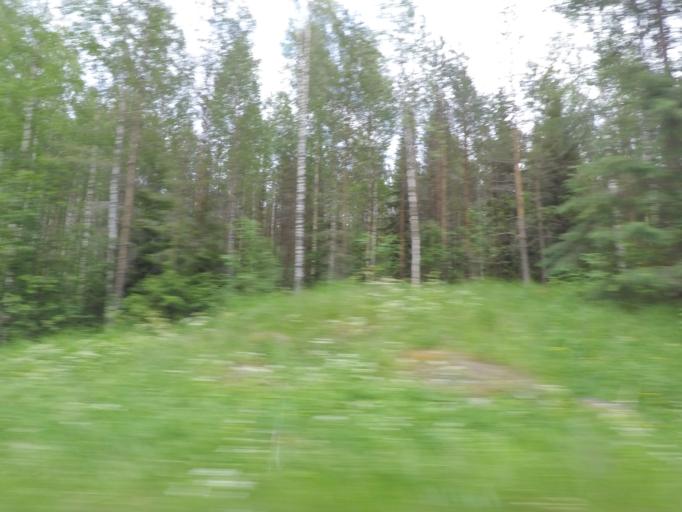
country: FI
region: Paijanne Tavastia
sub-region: Lahti
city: Hollola
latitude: 60.8177
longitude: 25.4839
